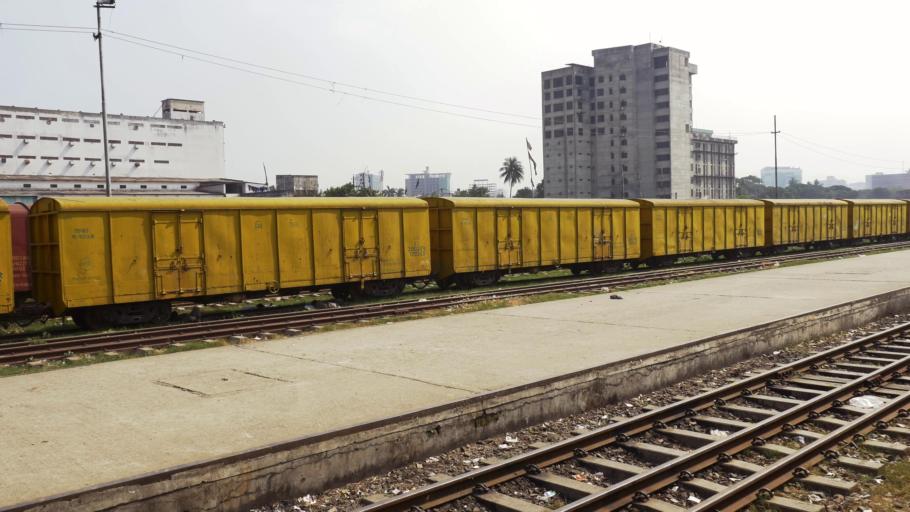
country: BD
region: Dhaka
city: Paltan
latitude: 23.7764
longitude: 90.3975
